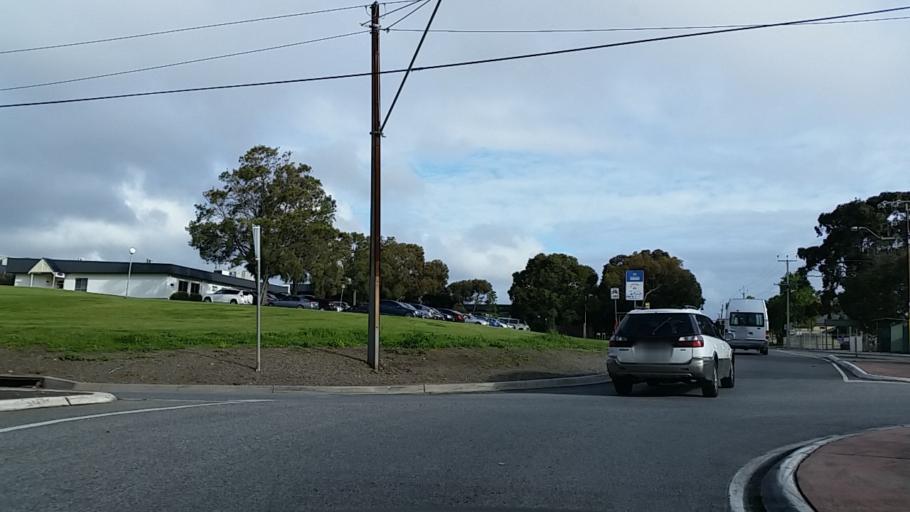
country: AU
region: South Australia
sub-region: Onkaparinga
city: Reynella
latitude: -35.1046
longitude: 138.5349
